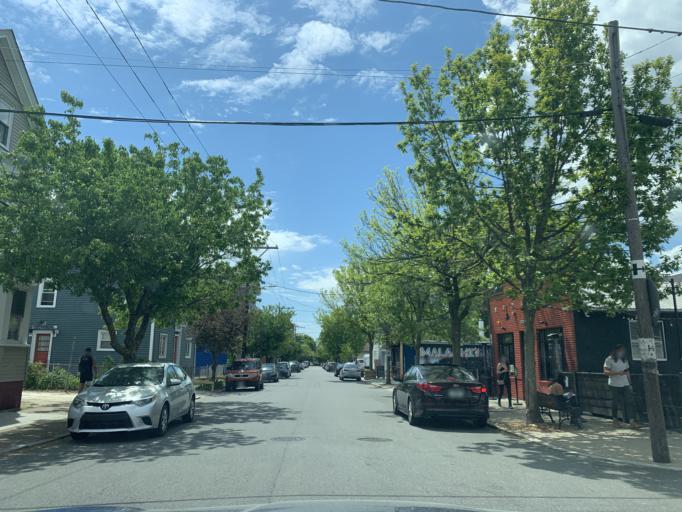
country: US
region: Rhode Island
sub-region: Providence County
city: Providence
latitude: 41.8224
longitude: -71.3921
